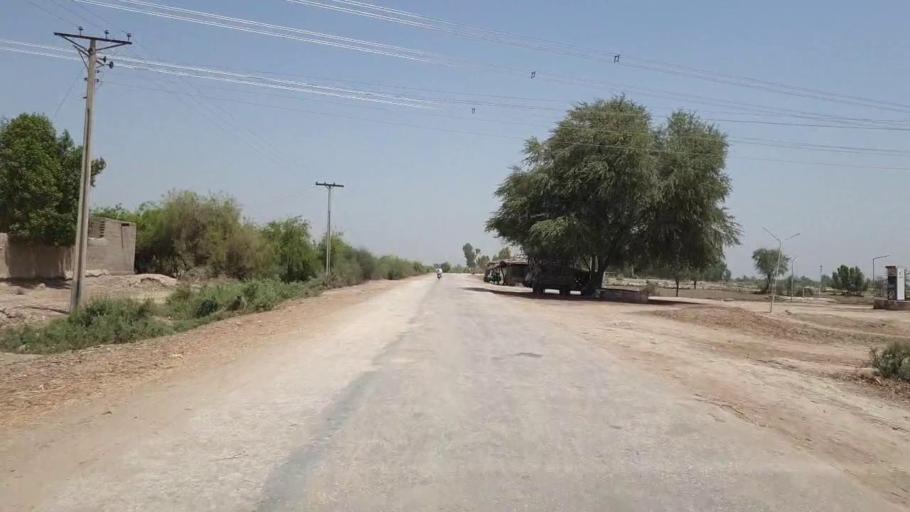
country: PK
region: Sindh
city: Adilpur
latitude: 27.8932
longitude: 69.2893
